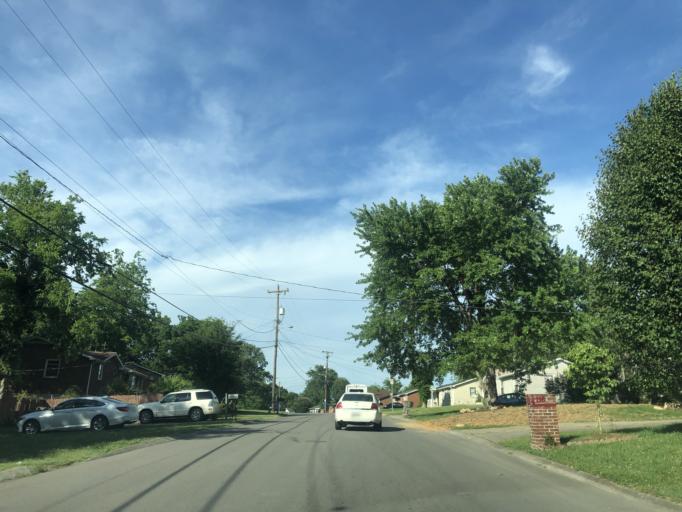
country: US
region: Tennessee
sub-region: Davidson County
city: Nashville
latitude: 36.2086
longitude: -86.8357
